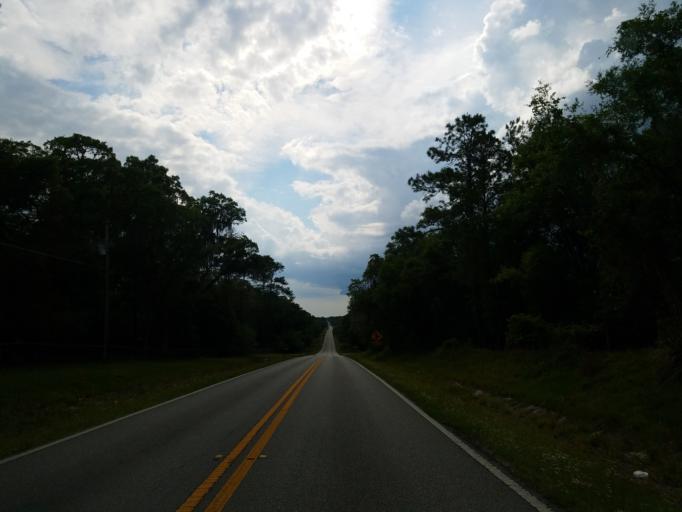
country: US
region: Florida
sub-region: Hernando County
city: Hill 'n Dale
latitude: 28.5535
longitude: -82.3086
